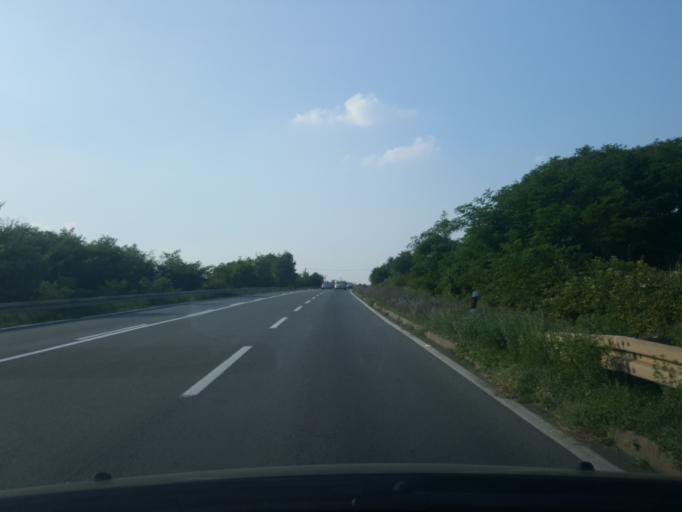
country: RS
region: Central Serbia
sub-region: Belgrade
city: Sopot
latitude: 44.5127
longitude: 20.6530
